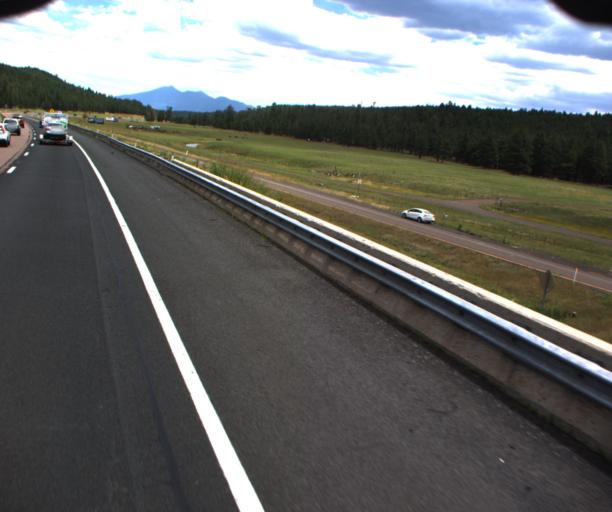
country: US
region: Arizona
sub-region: Coconino County
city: Mountainaire
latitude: 35.0184
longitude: -111.6845
